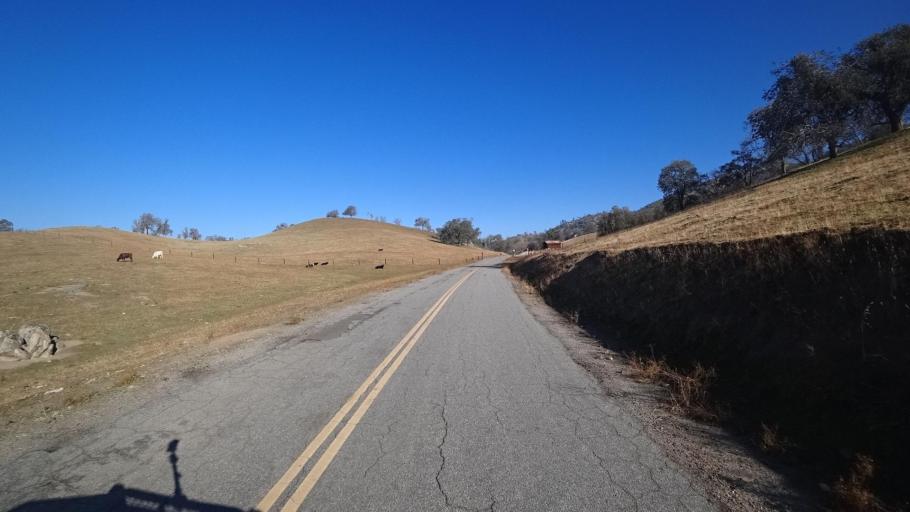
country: US
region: California
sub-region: Kern County
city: Alta Sierra
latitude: 35.7594
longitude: -118.8204
